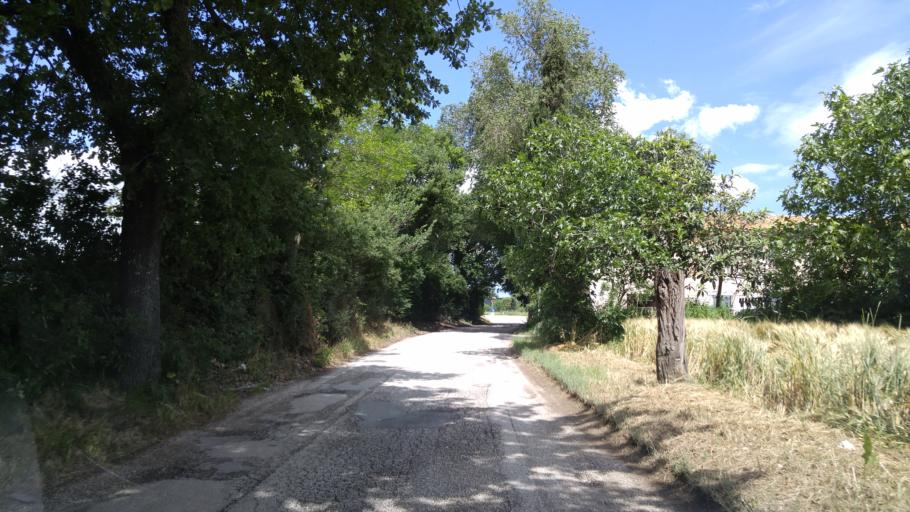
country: IT
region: The Marches
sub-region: Provincia di Pesaro e Urbino
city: Bellocchi
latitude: 43.8040
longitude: 13.0064
